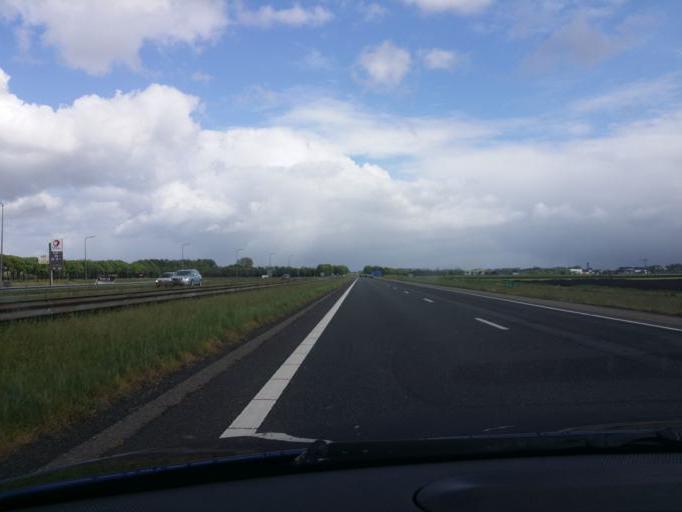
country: NL
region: Groningen
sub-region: Gemeente Hoogezand-Sappemeer
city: Hoogezand
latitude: 53.1870
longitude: 6.7157
